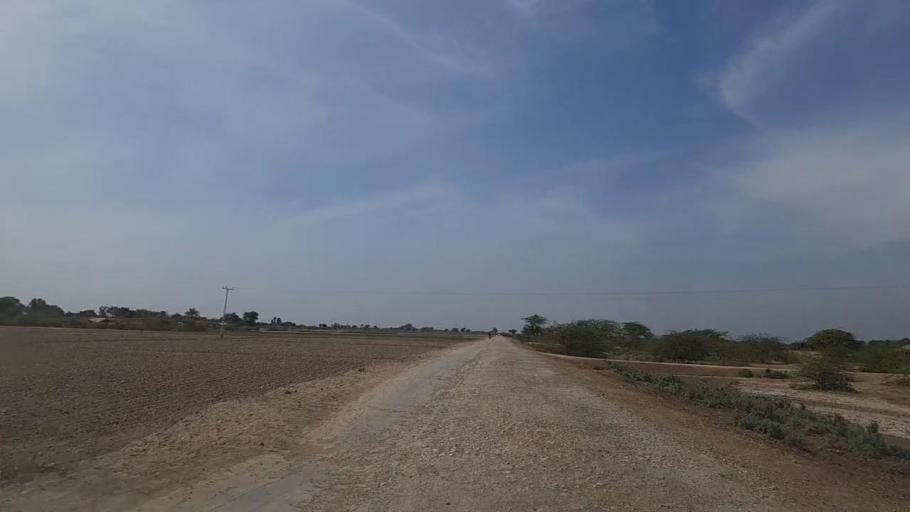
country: PK
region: Sindh
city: Kunri
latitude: 25.2127
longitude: 69.4967
